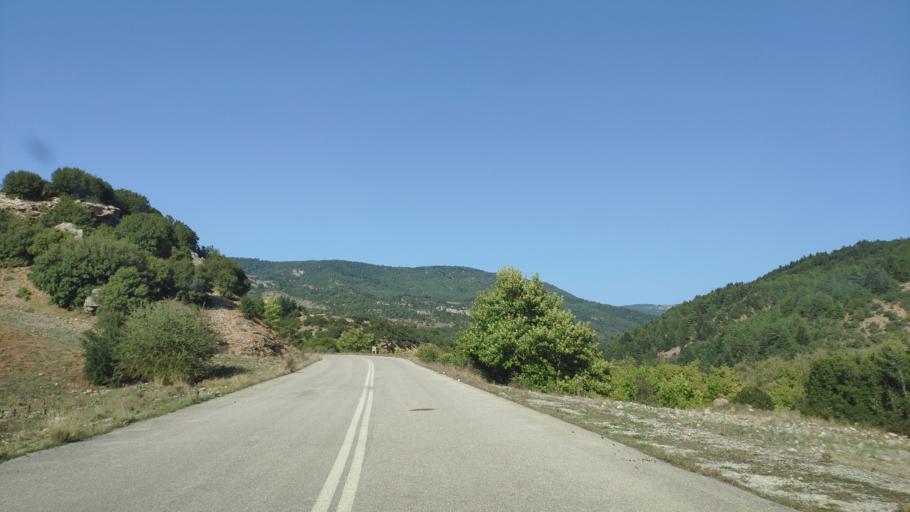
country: GR
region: West Greece
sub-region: Nomos Achaias
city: Aiyira
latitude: 37.9854
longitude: 22.3593
